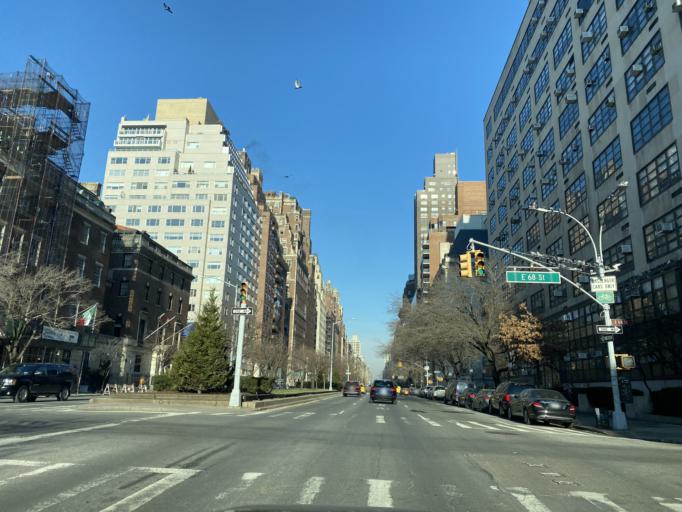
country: US
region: New York
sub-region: New York County
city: Manhattan
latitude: 40.7684
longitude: -73.9657
